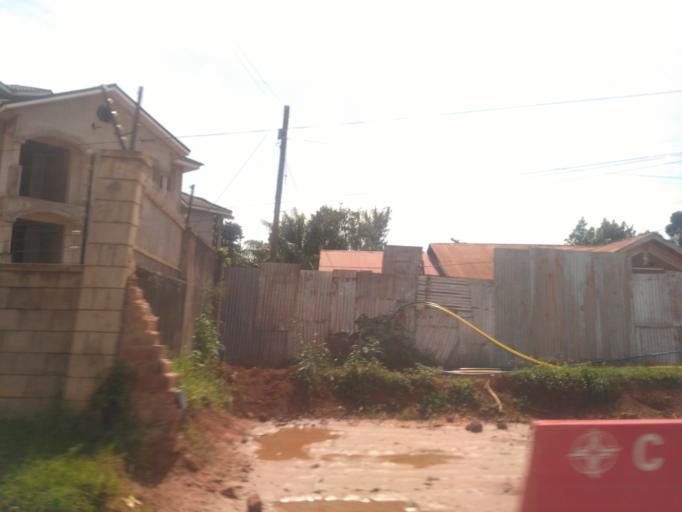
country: UG
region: Central Region
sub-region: Wakiso District
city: Entebbe
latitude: 0.0656
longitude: 32.4747
